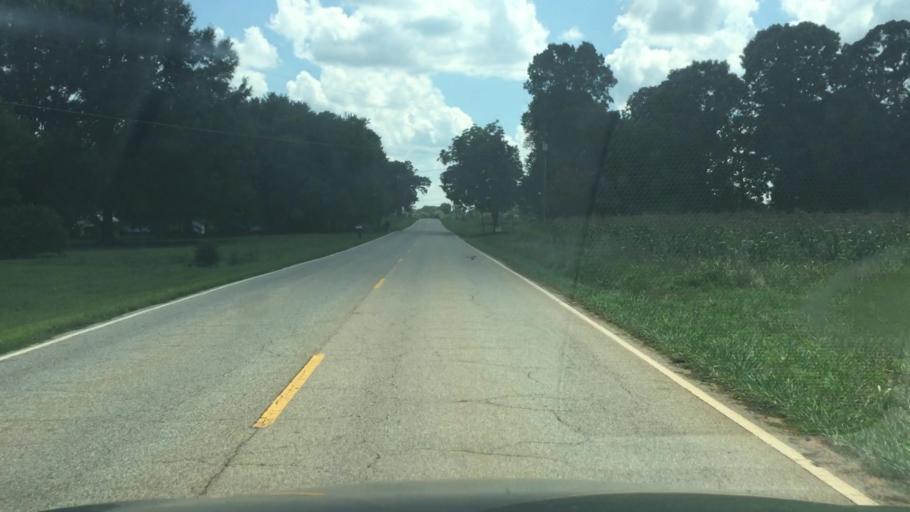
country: US
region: North Carolina
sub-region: Rowan County
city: China Grove
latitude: 35.6328
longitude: -80.6427
